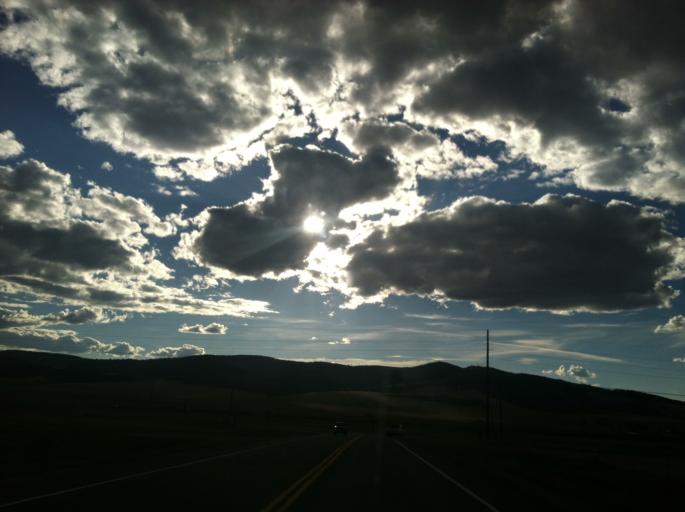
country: US
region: Montana
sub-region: Granite County
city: Philipsburg
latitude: 46.3349
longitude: -113.3090
